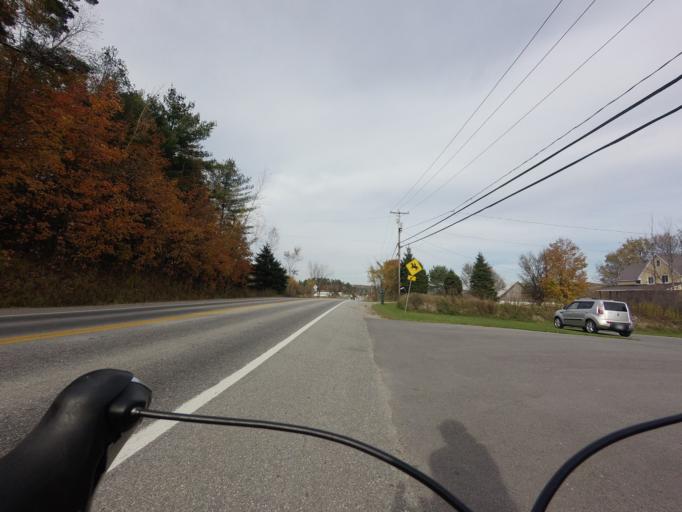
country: CA
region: Quebec
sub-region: Outaouais
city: Val-des-Monts
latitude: 45.5791
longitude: -75.6191
